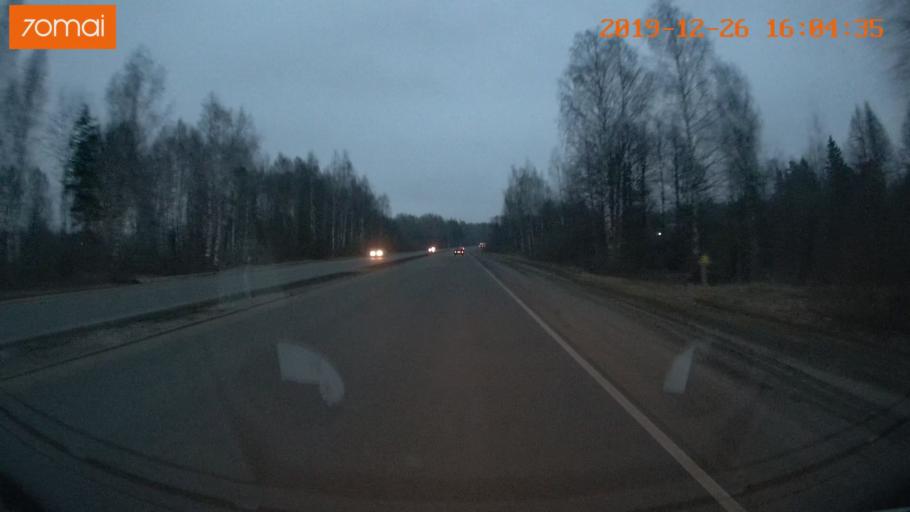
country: RU
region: Jaroslavl
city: Rybinsk
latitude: 58.0084
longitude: 38.8740
